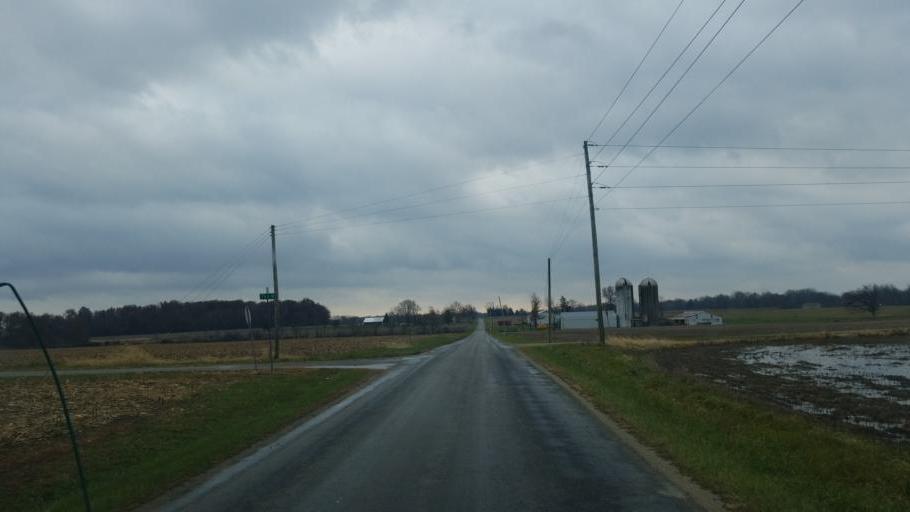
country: US
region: Indiana
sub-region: Adams County
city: Geneva
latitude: 40.5482
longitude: -84.9916
